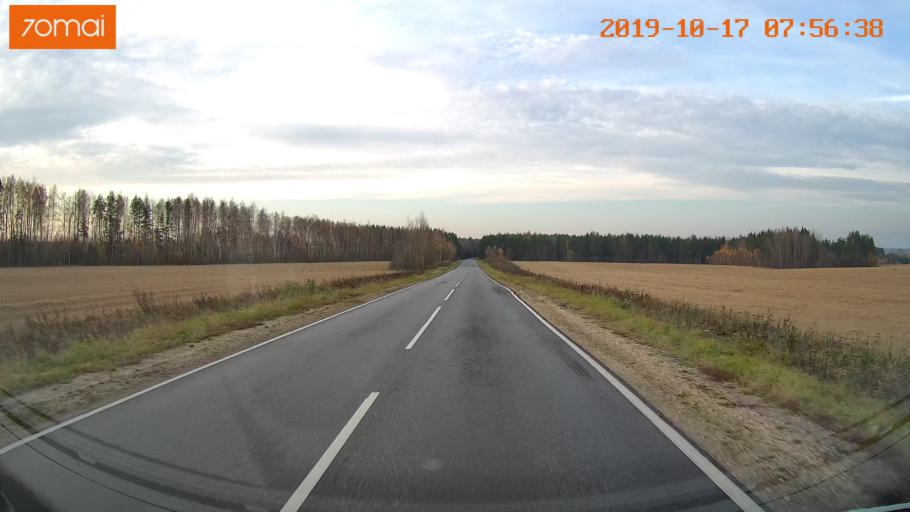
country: RU
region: Vladimir
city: Bavleny
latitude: 56.4206
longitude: 39.5880
